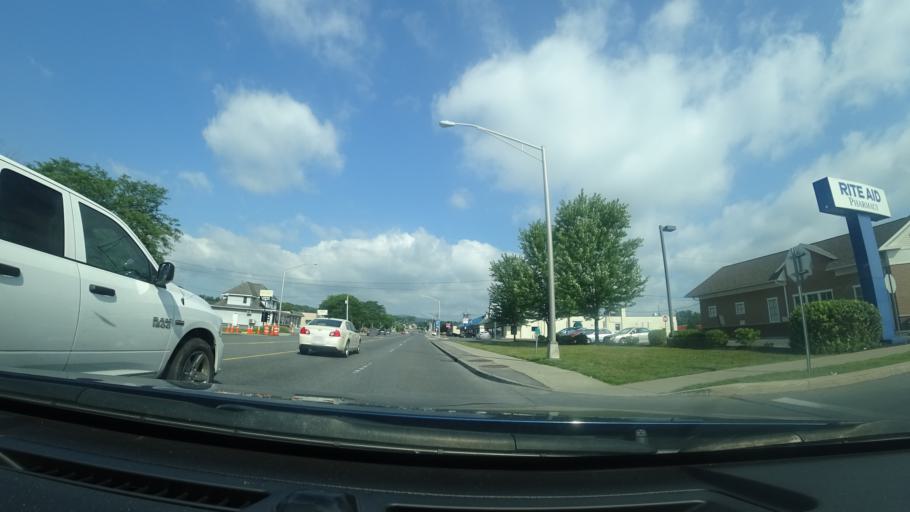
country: US
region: New York
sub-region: Warren County
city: Glens Falls North
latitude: 43.3277
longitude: -73.6679
